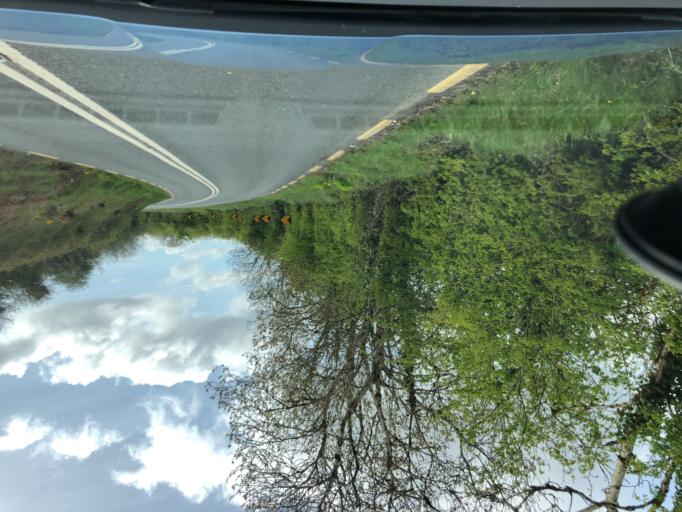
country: IE
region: Munster
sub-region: County Cork
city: Millstreet
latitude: 52.0699
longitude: -9.2902
